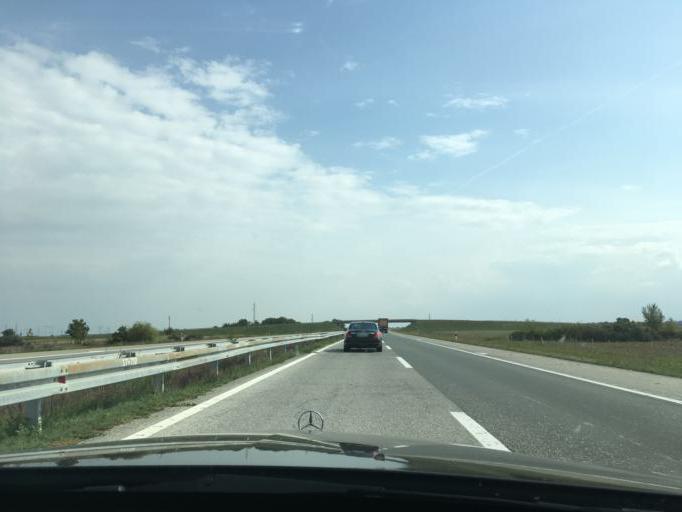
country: RS
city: Macvanska Mitrovica
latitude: 45.0145
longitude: 19.5716
